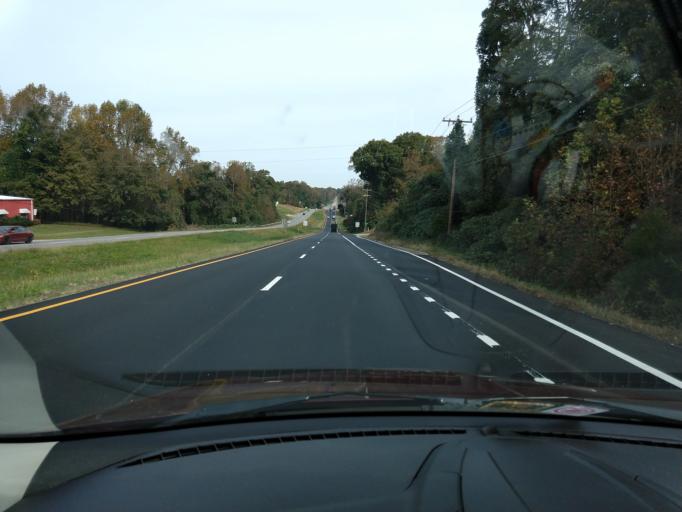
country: US
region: Virginia
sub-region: Pittsylvania County
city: Chatham
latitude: 36.7934
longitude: -79.3937
